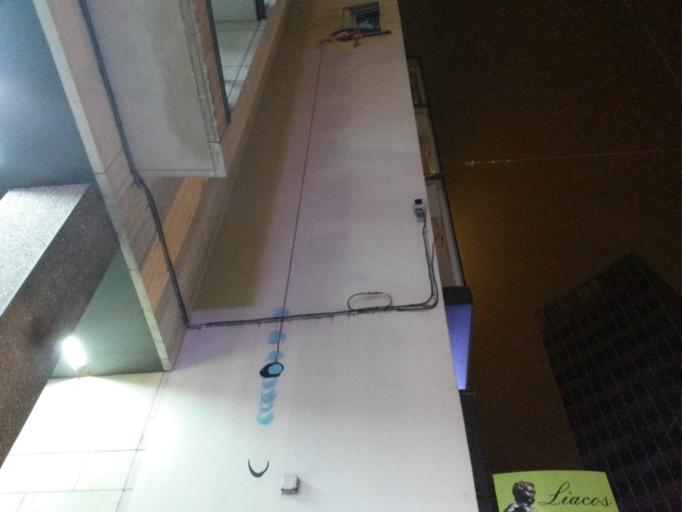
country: BE
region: Brussels Capital
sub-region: Bruxelles-Capitale
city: Brussels
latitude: 50.8499
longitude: 4.3533
